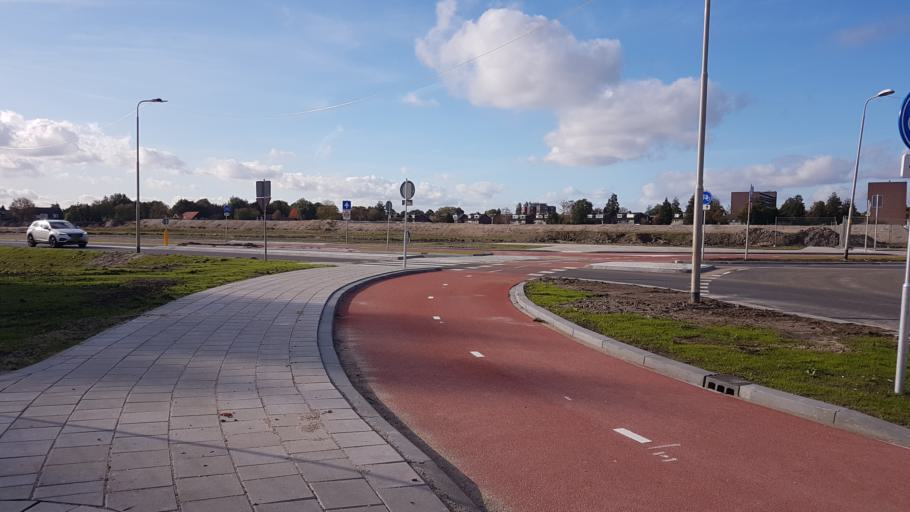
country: NL
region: South Holland
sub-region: Gemeente Hendrik-Ido-Ambacht
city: Hendrik-Ido-Ambacht
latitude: 51.8404
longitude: 4.6523
